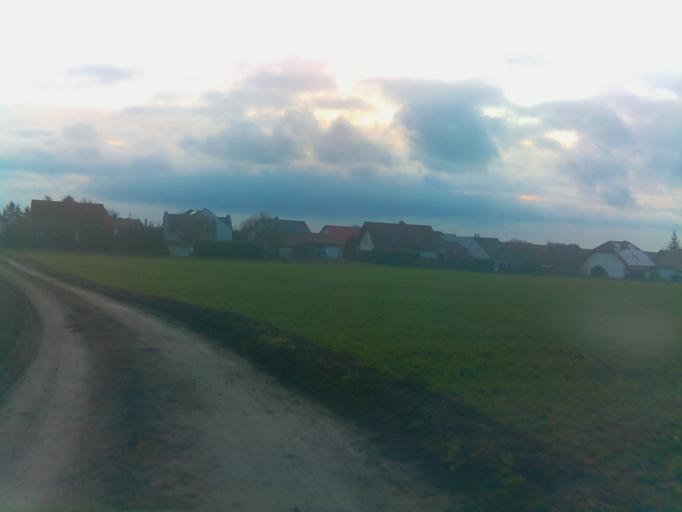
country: DE
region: Rheinland-Pfalz
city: Orbis
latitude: 49.6960
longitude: 7.9861
